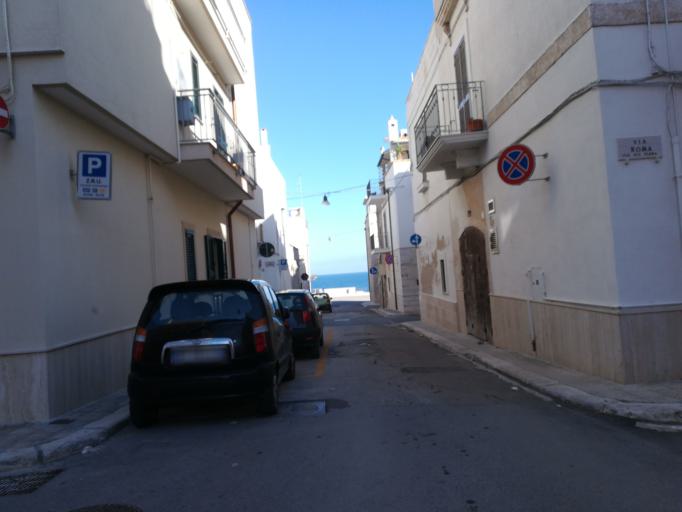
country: IT
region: Apulia
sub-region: Provincia di Bari
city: Polignano a Mare
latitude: 40.9957
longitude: 17.2243
